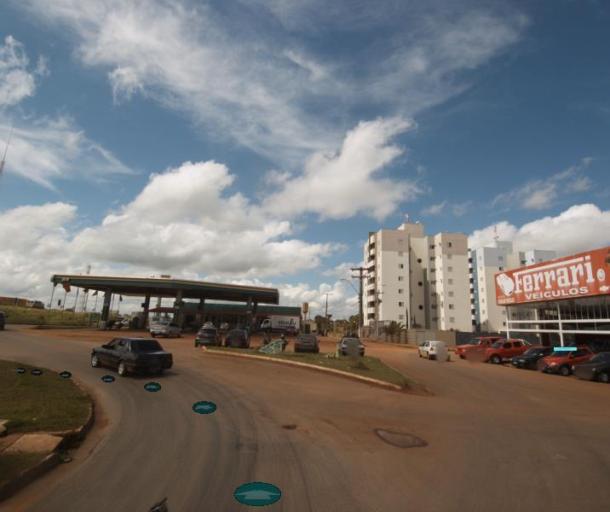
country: BR
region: Federal District
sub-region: Brasilia
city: Brasilia
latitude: -15.7522
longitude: -48.2606
